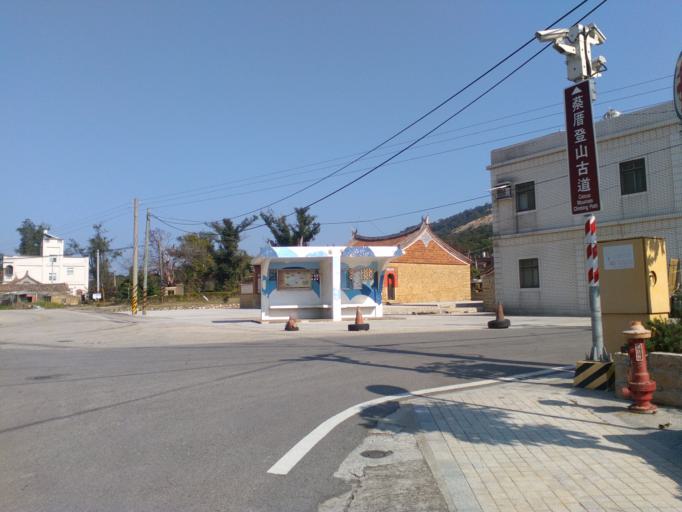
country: TW
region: Fukien
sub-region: Kinmen
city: Jincheng
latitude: 24.4733
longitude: 118.4165
